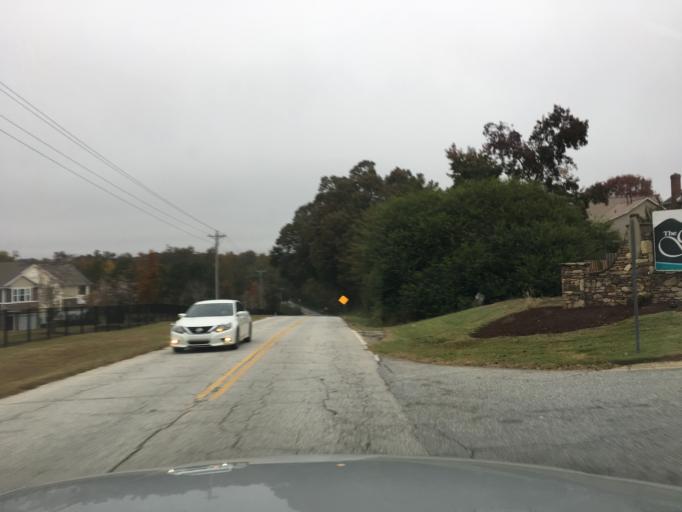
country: US
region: South Carolina
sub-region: Greenville County
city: Five Forks
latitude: 34.8227
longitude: -82.2689
